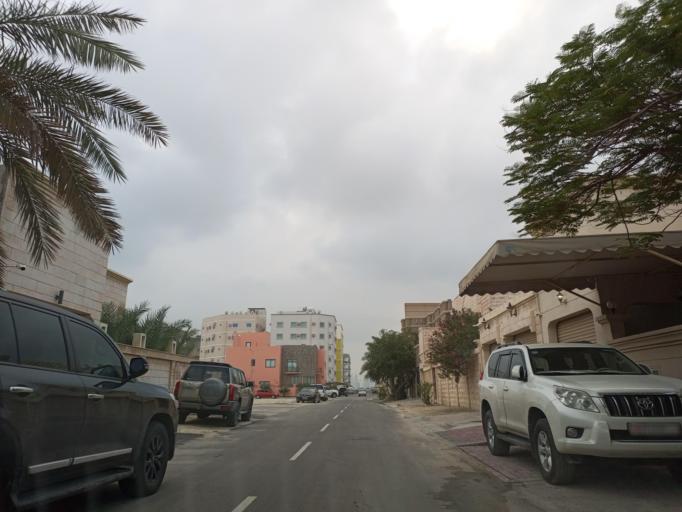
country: BH
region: Muharraq
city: Al Hadd
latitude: 26.2411
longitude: 50.6490
